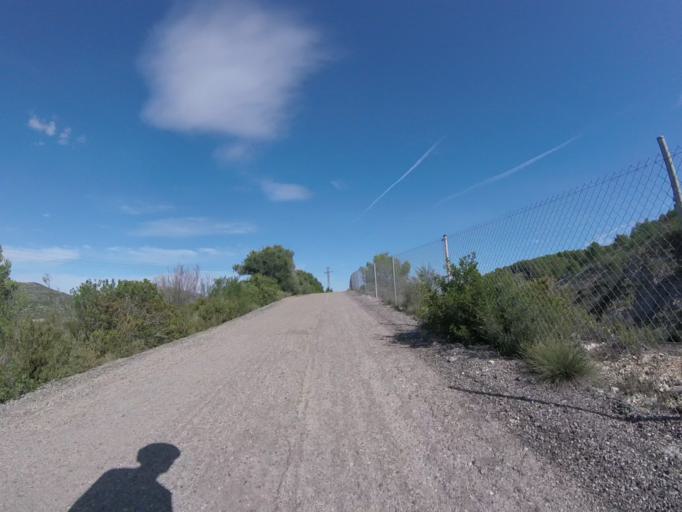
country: ES
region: Valencia
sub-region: Provincia de Castello
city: Santa Magdalena de Pulpis
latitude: 40.3839
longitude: 0.3431
